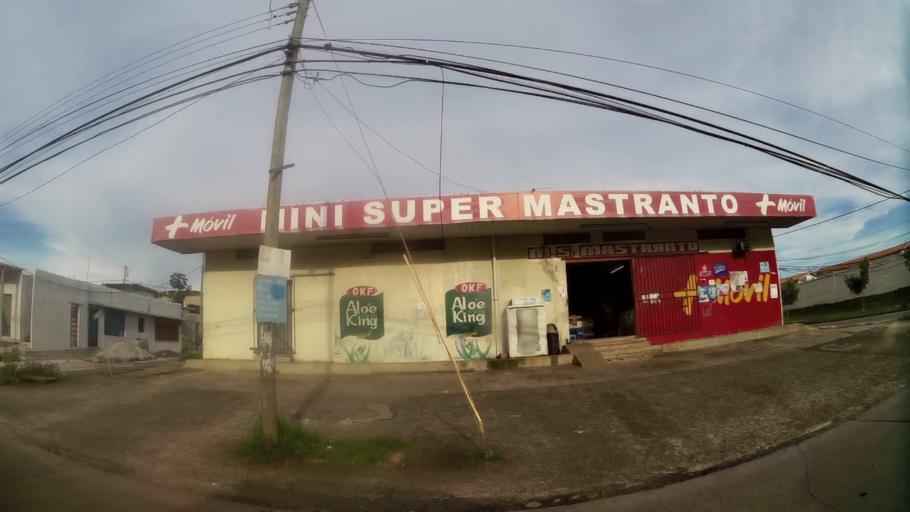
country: PA
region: Panama
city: La Chorrera
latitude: 8.8940
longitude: -79.7658
